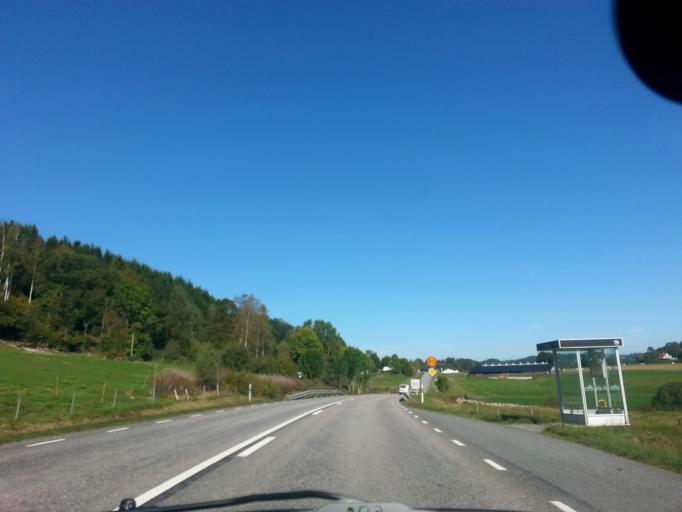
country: SE
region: Vaestra Goetaland
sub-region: Harryda Kommun
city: Ravlanda
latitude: 57.5383
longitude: 12.5313
